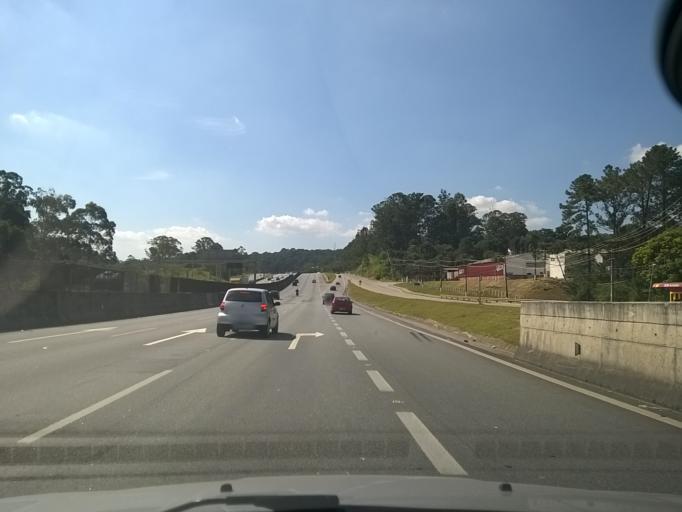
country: BR
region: Sao Paulo
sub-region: Caieiras
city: Caieiras
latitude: -23.4293
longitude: -46.7871
